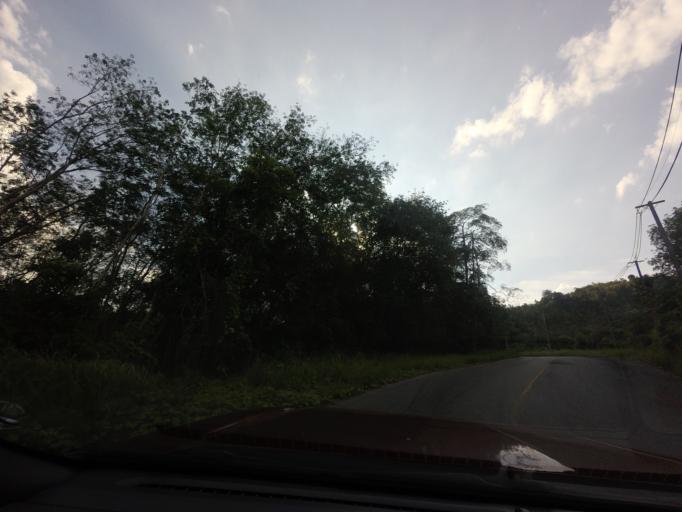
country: TH
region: Yala
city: Than To
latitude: 6.1424
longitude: 101.2877
